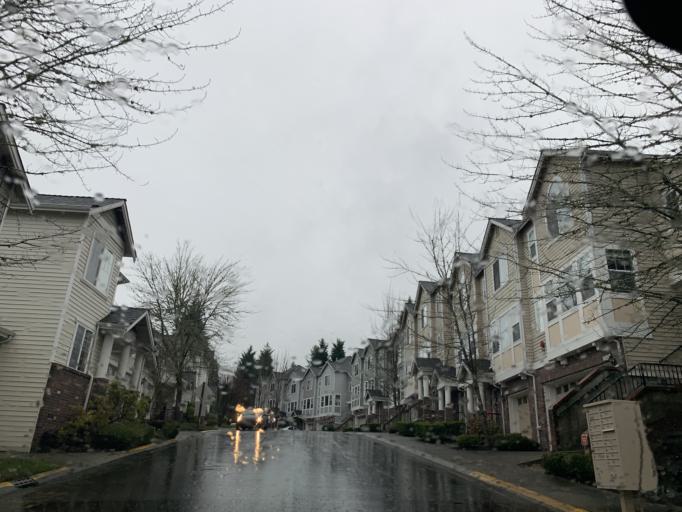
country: US
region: Washington
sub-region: King County
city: Woodinville
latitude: 47.7400
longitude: -122.1617
